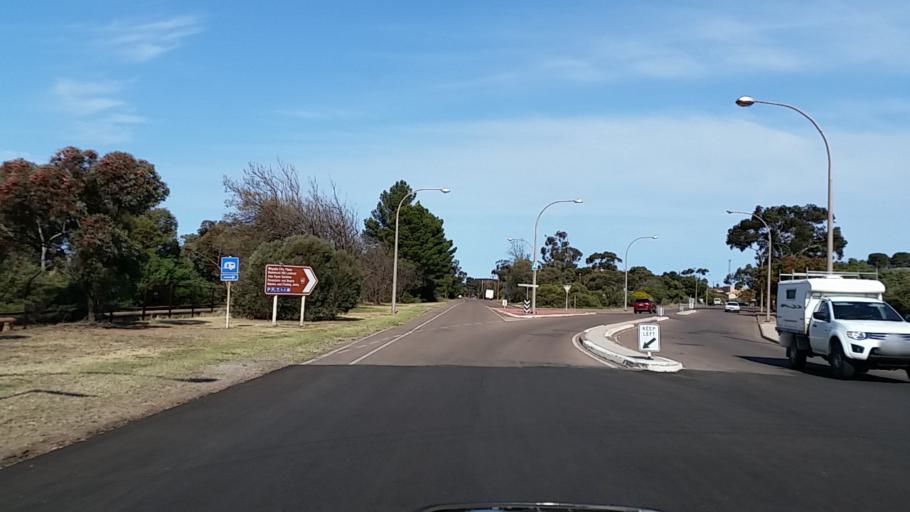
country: AU
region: South Australia
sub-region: Whyalla
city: Whyalla
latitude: -33.0296
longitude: 137.5816
